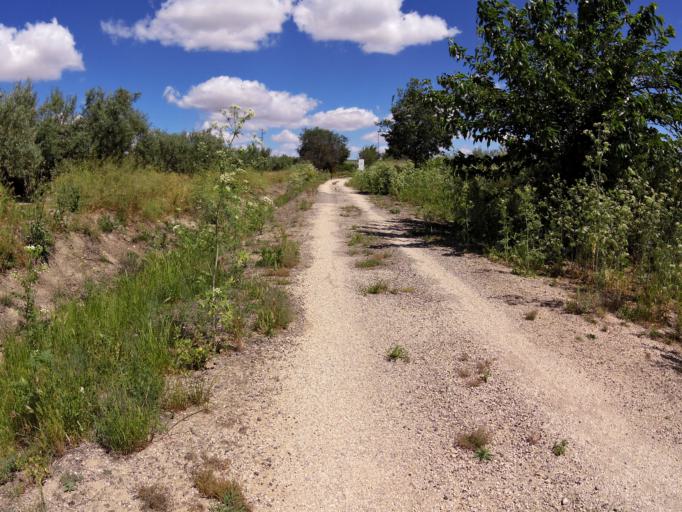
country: ES
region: Andalusia
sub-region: Provincia de Jaen
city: Alcaudete
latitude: 37.6596
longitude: -4.0626
